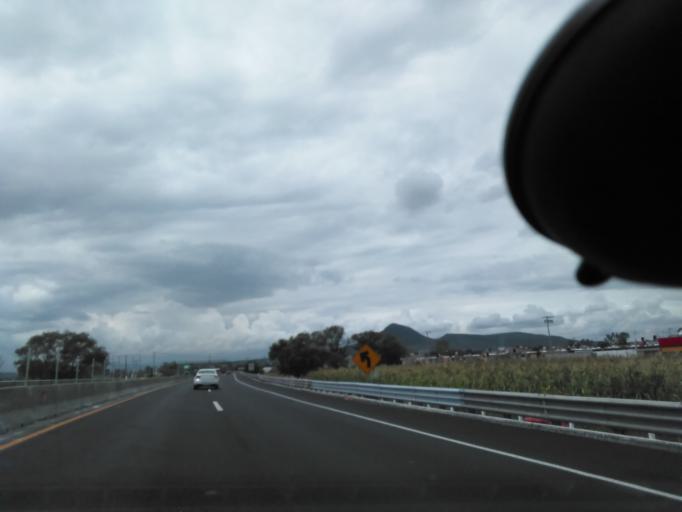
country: MX
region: Mexico
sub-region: Huehuetoca
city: Casa Nueva
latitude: 19.8208
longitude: -99.2083
